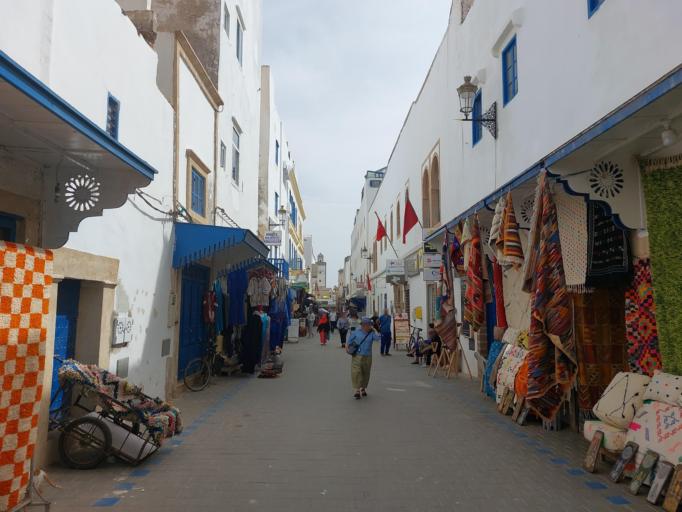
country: MA
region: Marrakech-Tensift-Al Haouz
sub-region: Essaouira
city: Essaouira
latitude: 31.5141
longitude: -9.7716
